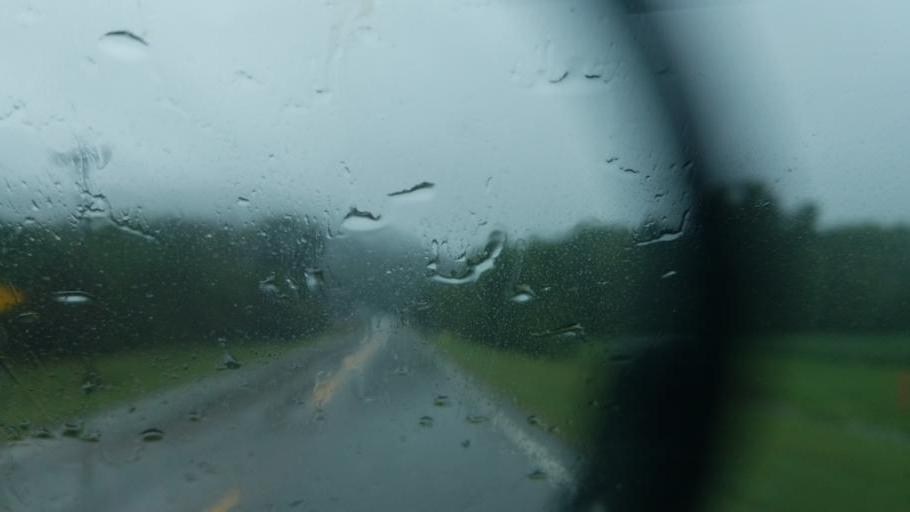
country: US
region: Kentucky
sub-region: Rowan County
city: Morehead
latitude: 38.3110
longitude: -83.5679
